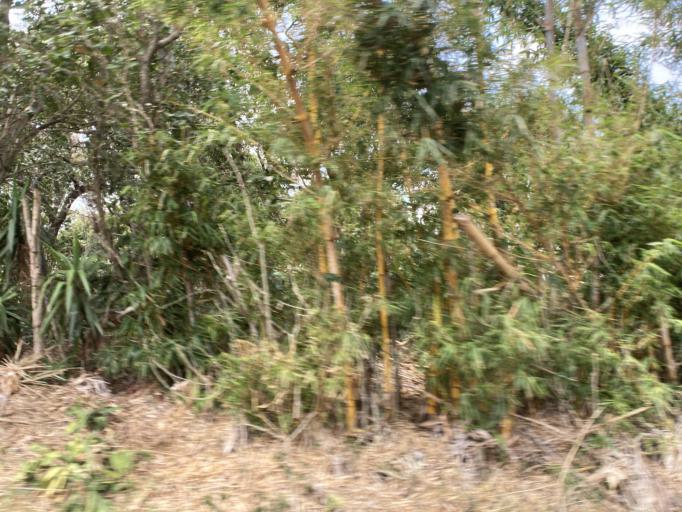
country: GT
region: Escuintla
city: San Vicente Pacaya
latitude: 14.3461
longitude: -90.5710
